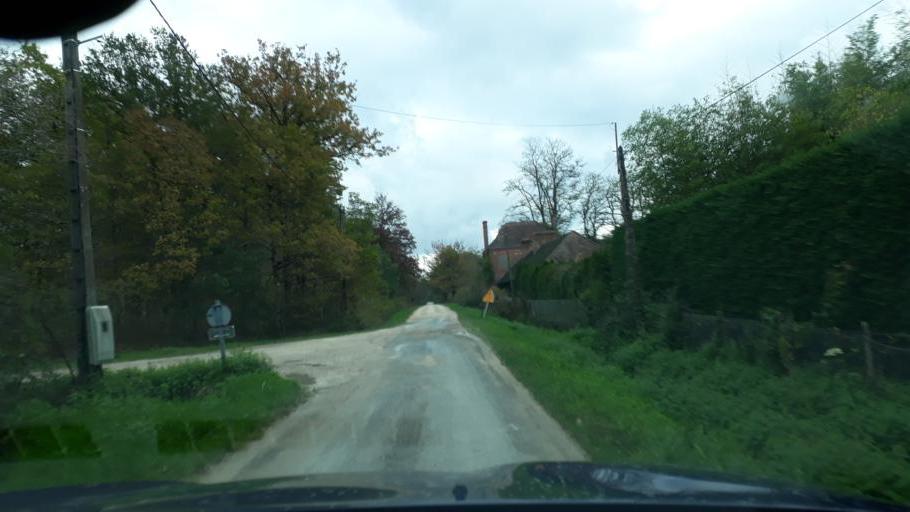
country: FR
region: Centre
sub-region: Departement du Loiret
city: Bray-en-Val
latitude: 47.8196
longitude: 2.4128
